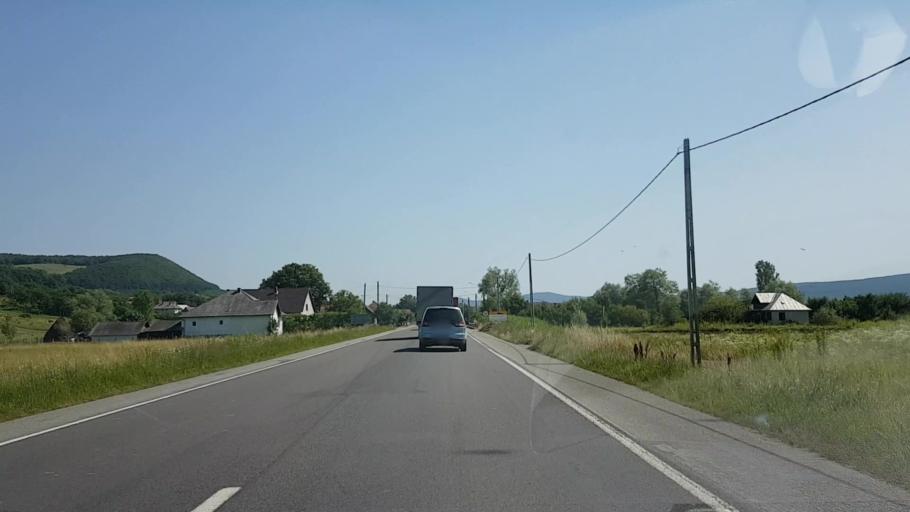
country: RO
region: Bistrita-Nasaud
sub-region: Comuna Sieu-Odorhei
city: Sieu-Odorhei
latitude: 47.1562
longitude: 24.3065
